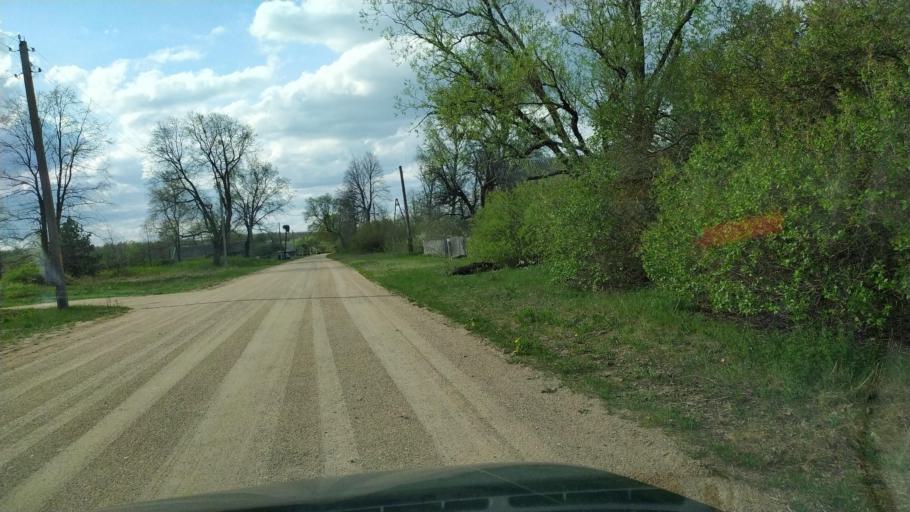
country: BY
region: Brest
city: Pruzhany
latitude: 52.7042
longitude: 24.2637
